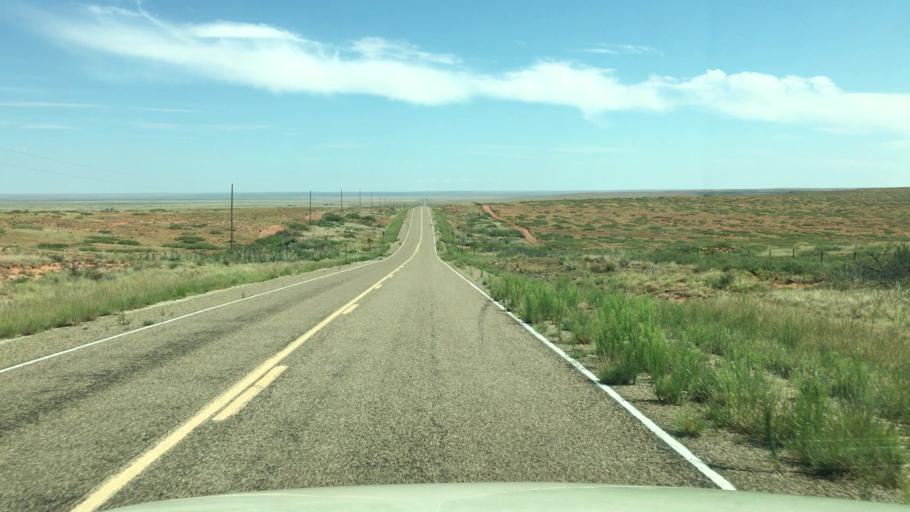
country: US
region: New Mexico
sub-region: Chaves County
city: Roswell
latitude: 33.9717
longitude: -104.5788
